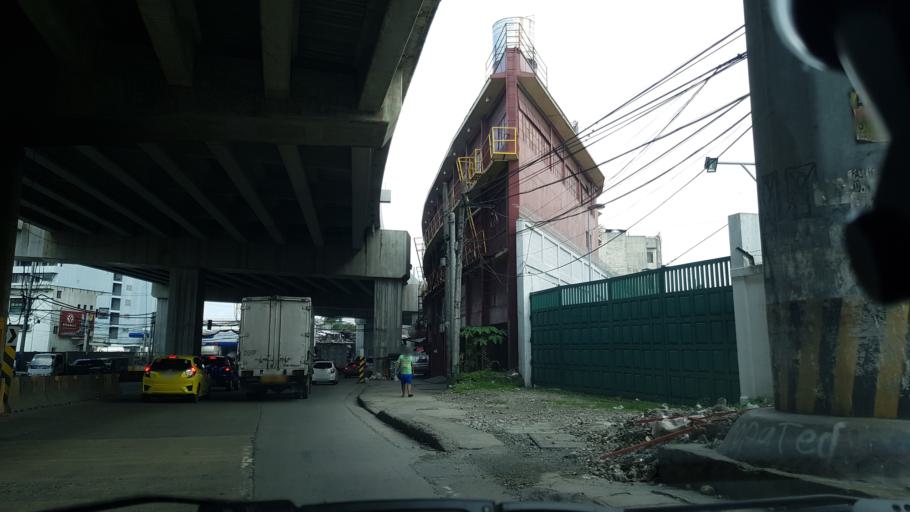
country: PH
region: Calabarzon
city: Del Monte
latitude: 14.6178
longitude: 121.0154
